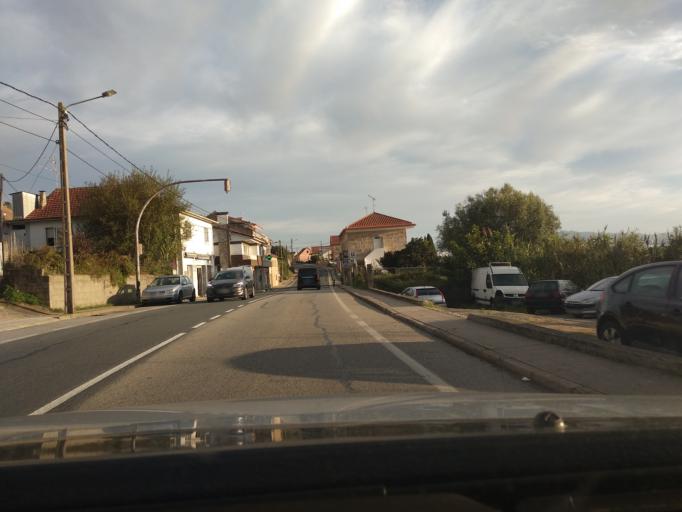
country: ES
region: Galicia
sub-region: Provincia de Pontevedra
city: Moana
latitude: 42.2889
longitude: -8.7168
